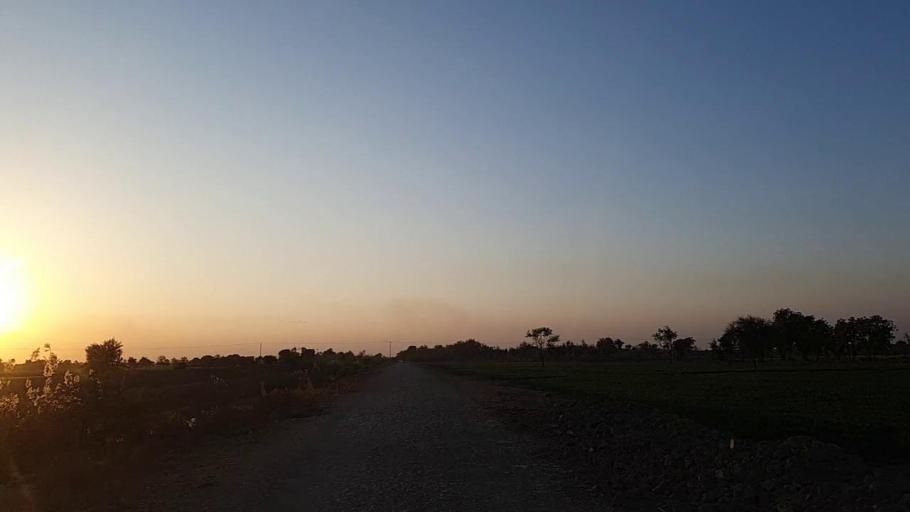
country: PK
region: Sindh
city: Jam Sahib
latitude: 26.3109
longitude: 68.6563
